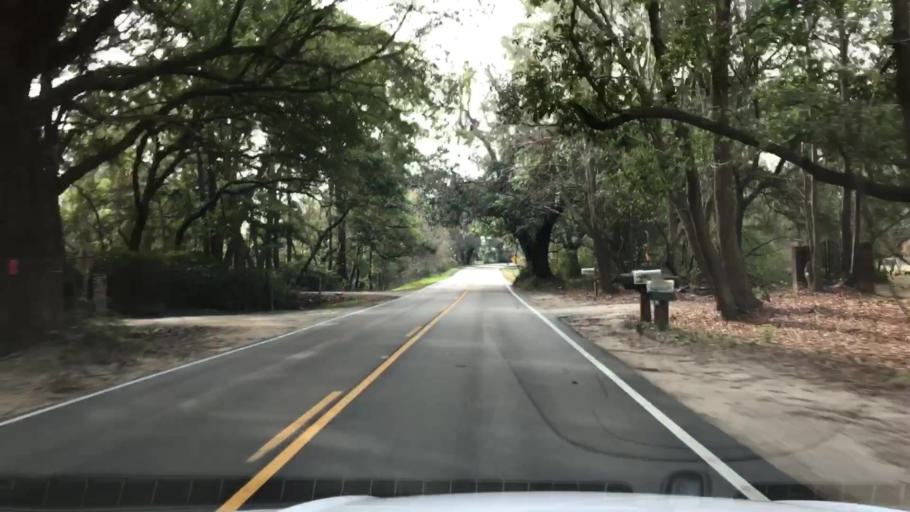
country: US
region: South Carolina
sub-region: Charleston County
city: Folly Beach
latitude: 32.6931
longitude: -80.0161
